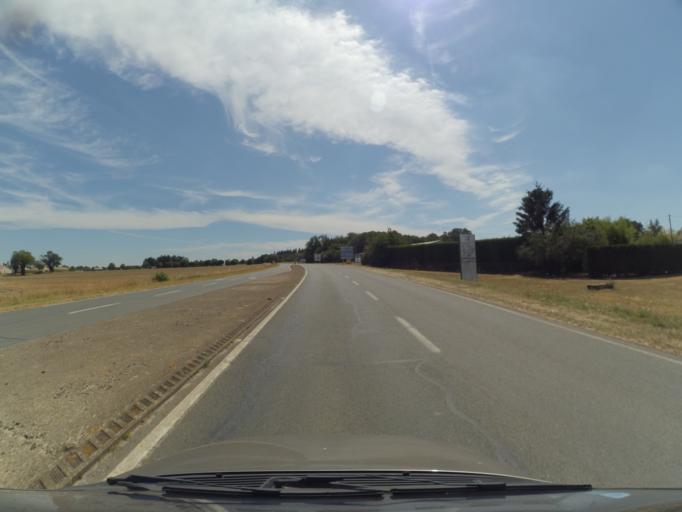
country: FR
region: Poitou-Charentes
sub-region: Departement de la Vienne
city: Lusignan
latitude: 46.4296
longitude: 0.1086
